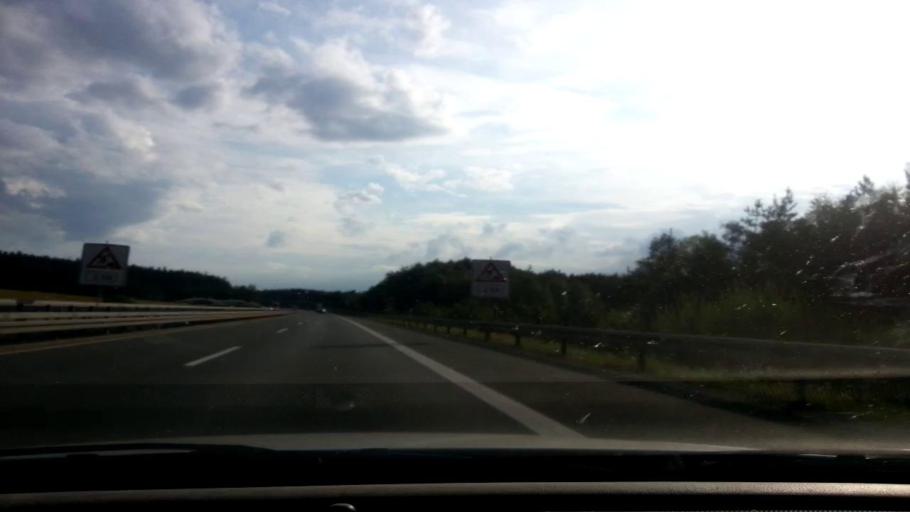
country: DE
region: Bavaria
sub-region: Upper Palatinate
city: Wiesau
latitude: 49.8754
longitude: 12.1943
